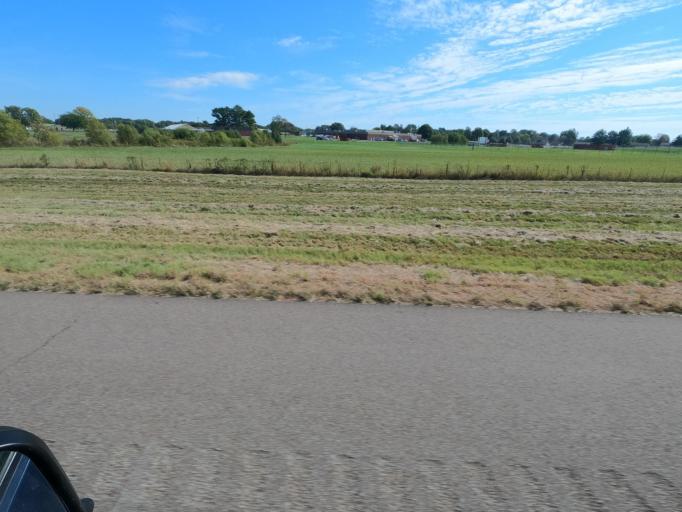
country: US
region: Tennessee
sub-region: Dyer County
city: Newbern
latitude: 36.1161
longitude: -89.2863
